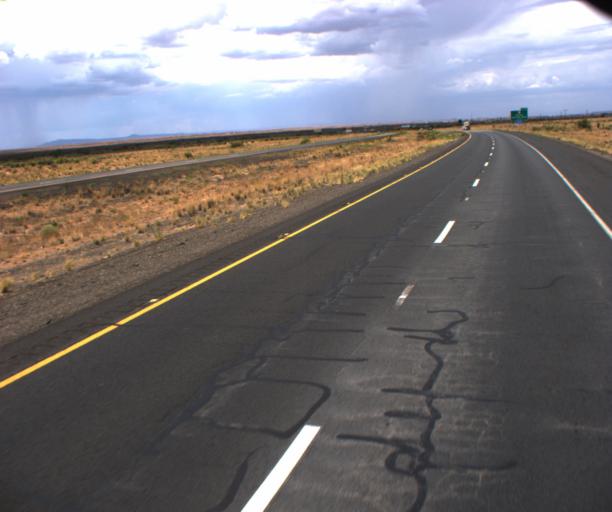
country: US
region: Arizona
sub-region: Navajo County
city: Winslow
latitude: 35.0065
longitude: -110.6172
